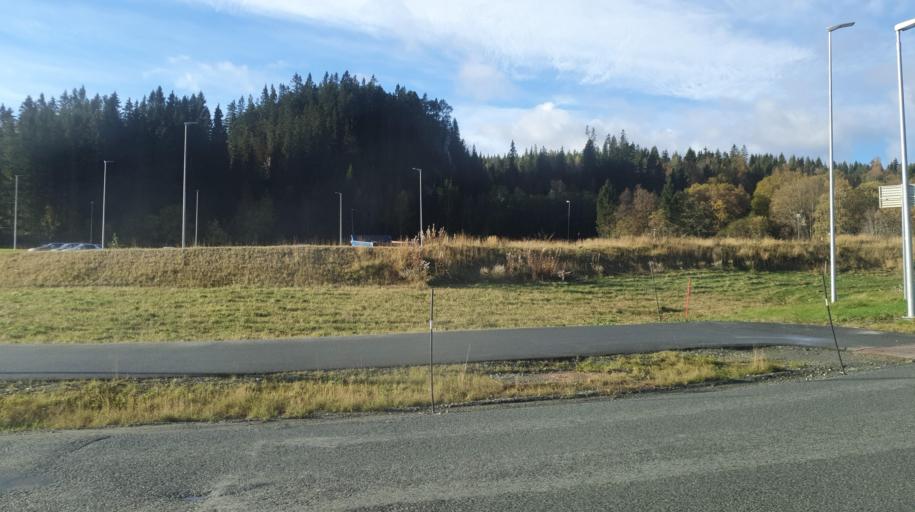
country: NO
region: Sor-Trondelag
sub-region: Klaebu
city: Klaebu
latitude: 63.3132
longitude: 10.4307
